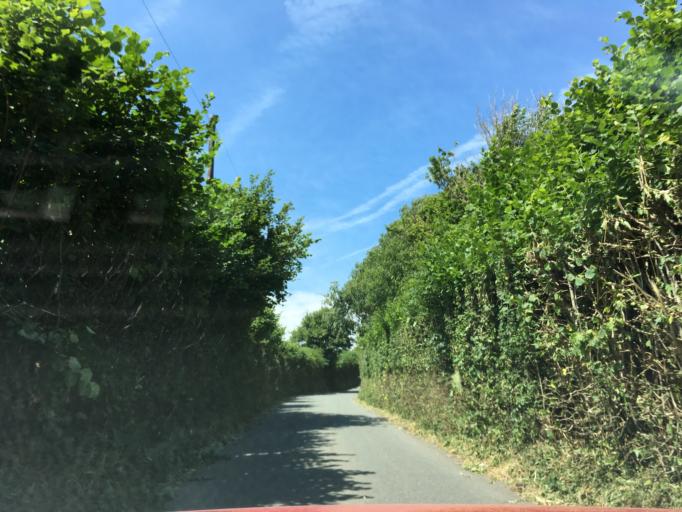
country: GB
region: Wales
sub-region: Caerphilly County Borough
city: Machen
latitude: 51.5508
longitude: -3.1421
